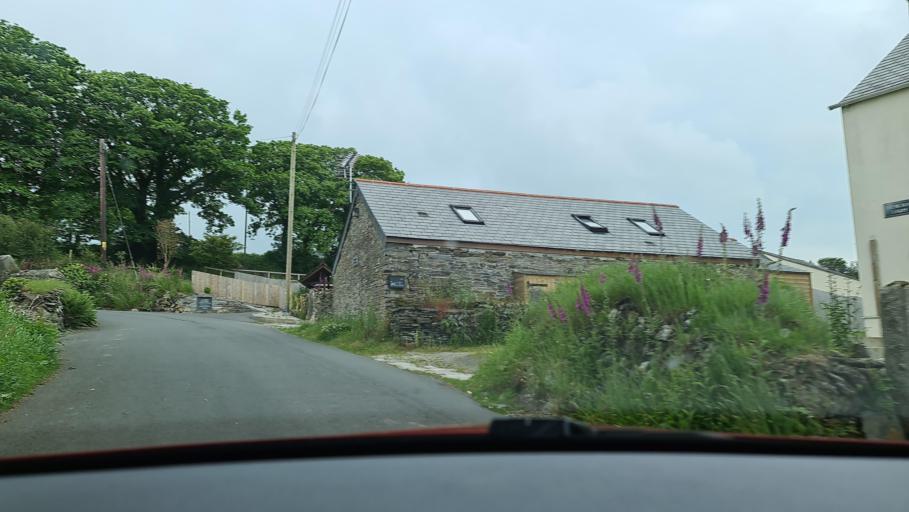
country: GB
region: England
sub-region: Cornwall
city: Camelford
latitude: 50.6209
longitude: -4.6991
